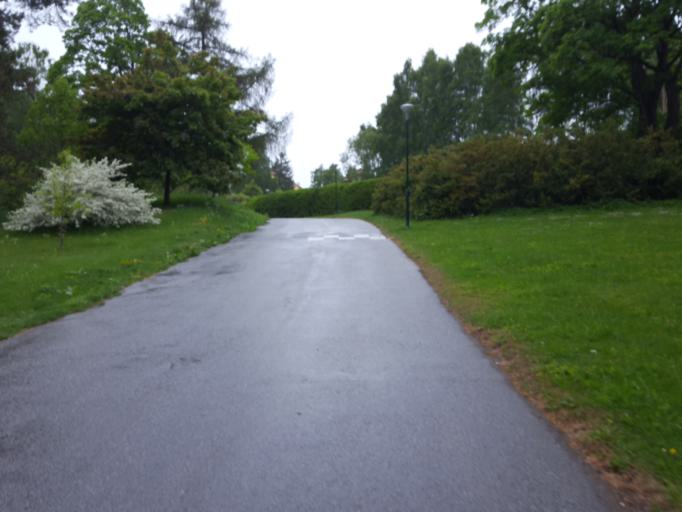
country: SE
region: Stockholm
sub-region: Solna Kommun
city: Solna
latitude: 59.3601
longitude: 18.0212
